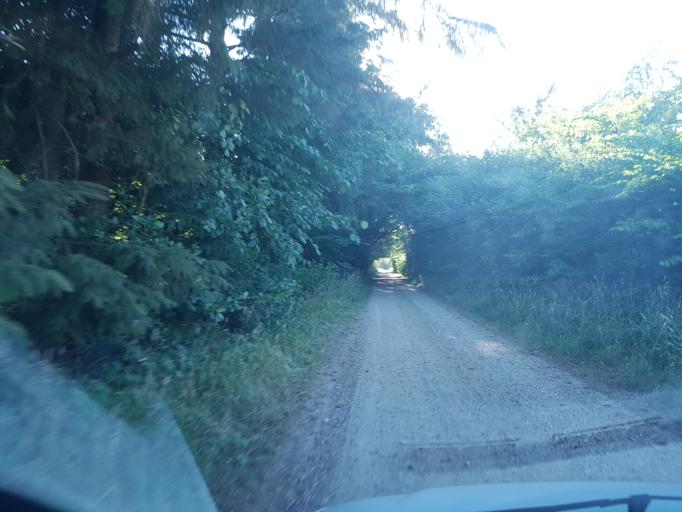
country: DK
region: South Denmark
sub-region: Esbjerg Kommune
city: Esbjerg
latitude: 55.4943
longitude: 8.5112
